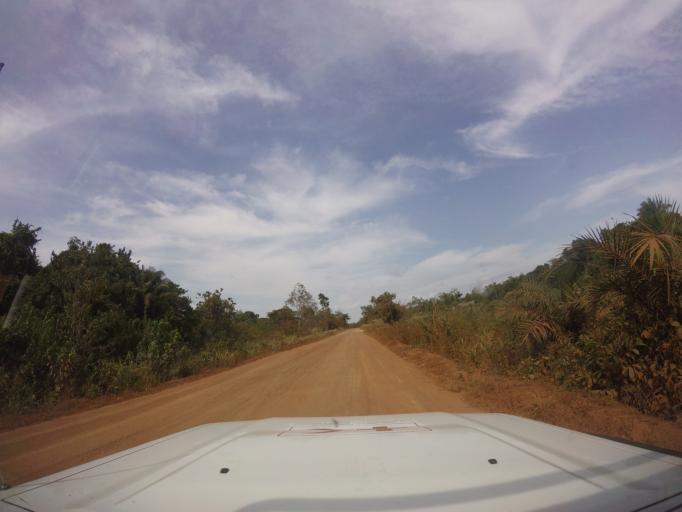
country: LR
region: Grand Cape Mount
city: Robertsport
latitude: 6.6997
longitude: -11.0956
